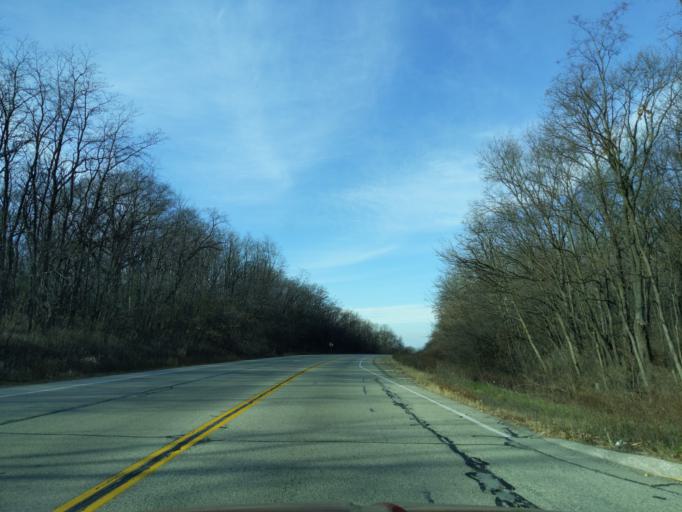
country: US
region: Wisconsin
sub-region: Walworth County
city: Whitewater
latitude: 42.7998
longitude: -88.6465
